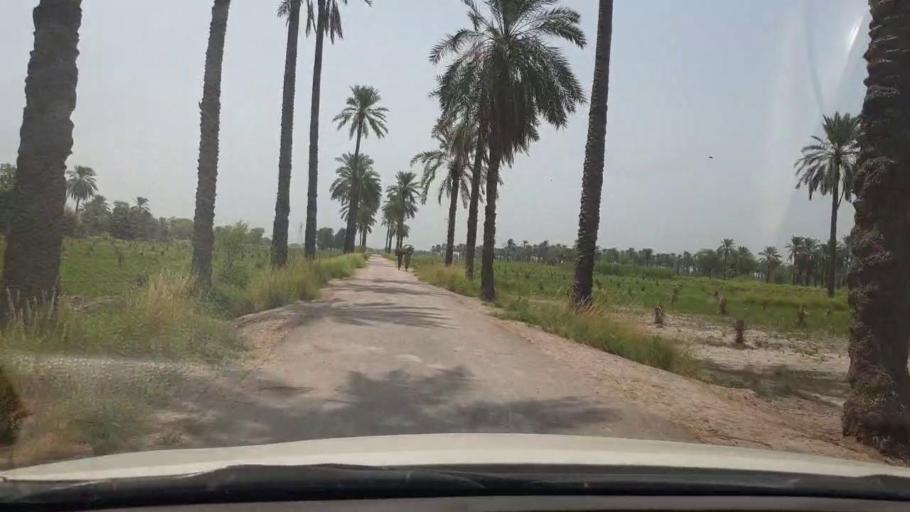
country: PK
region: Sindh
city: Shikarpur
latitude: 28.0212
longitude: 68.6169
